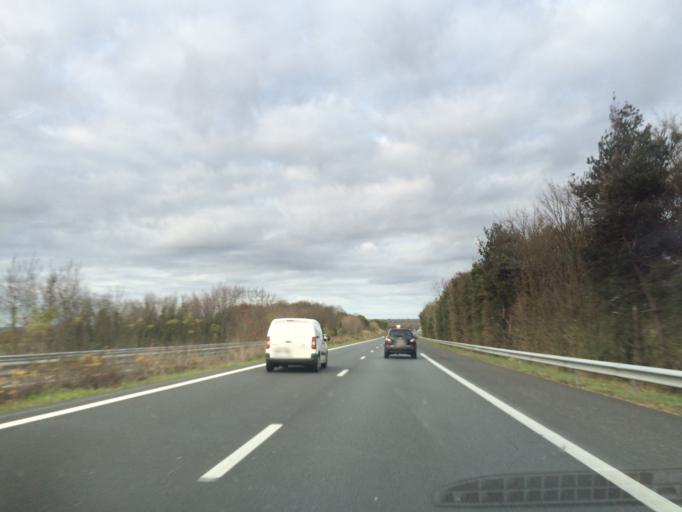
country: FR
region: Poitou-Charentes
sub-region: Departement de la Charente-Maritime
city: Saint-Jean-d'Angely
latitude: 46.0516
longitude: -0.5370
